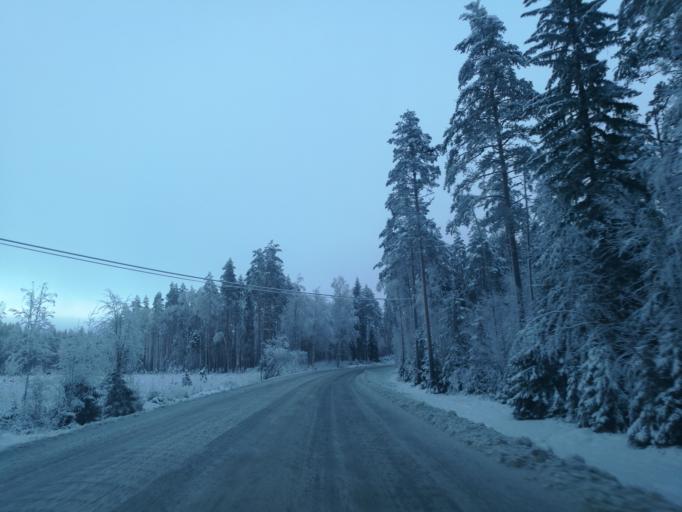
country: NO
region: Hedmark
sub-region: Grue
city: Kirkenaer
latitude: 60.2880
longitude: 12.1915
